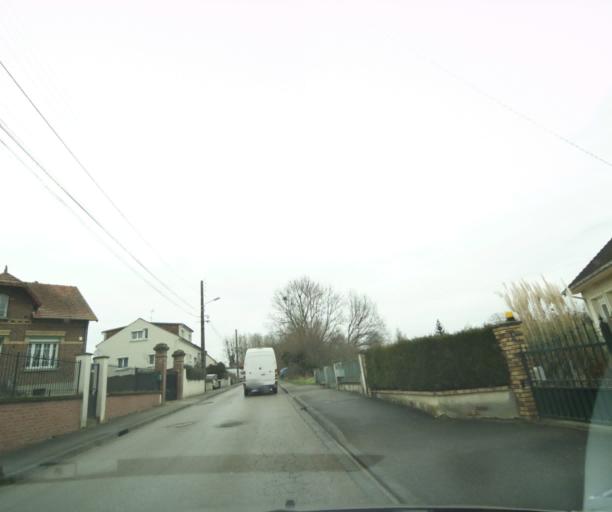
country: FR
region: Picardie
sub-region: Departement de l'Oise
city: Noyon
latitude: 49.5937
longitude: 3.0128
